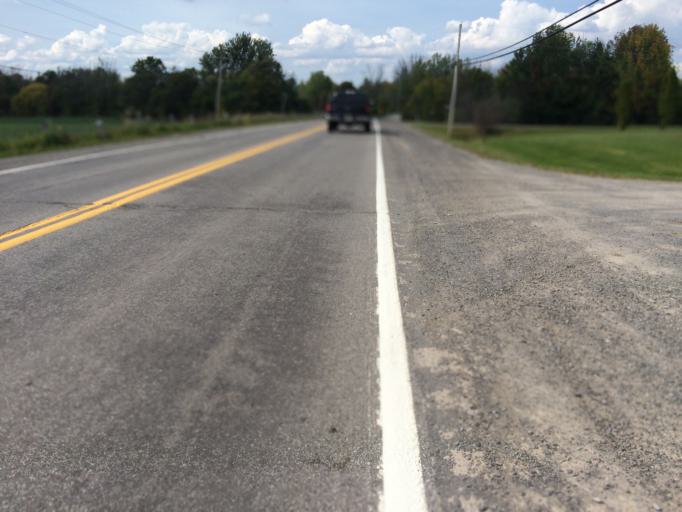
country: CA
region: Ontario
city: Bells Corners
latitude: 45.2052
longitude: -75.6530
